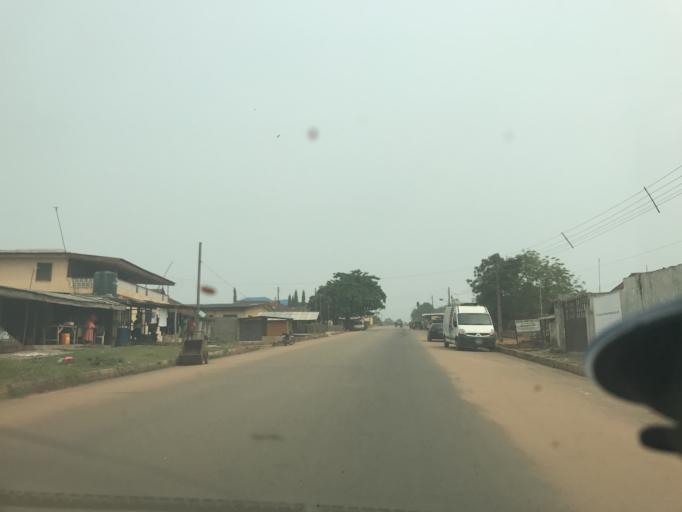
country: NG
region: Ogun
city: Ilaro
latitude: 6.8931
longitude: 3.0173
